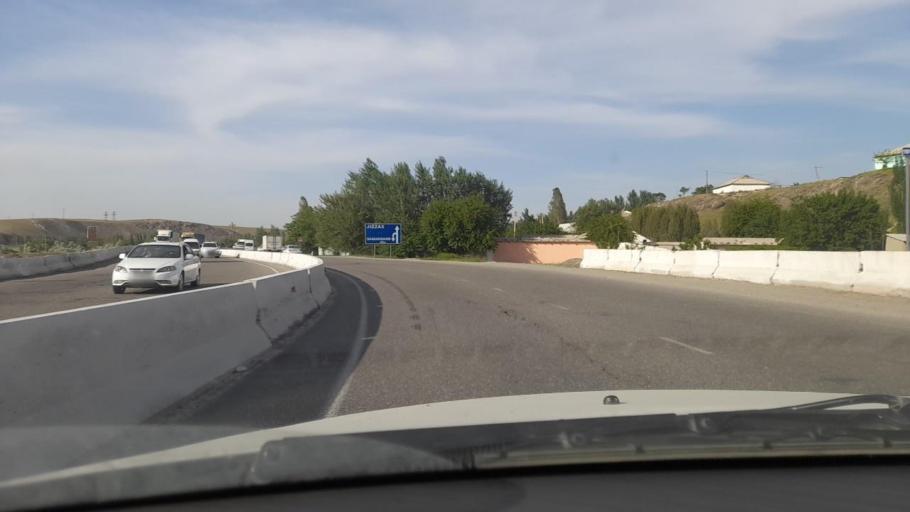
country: UZ
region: Jizzax
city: Jizzax
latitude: 40.0272
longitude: 67.6179
